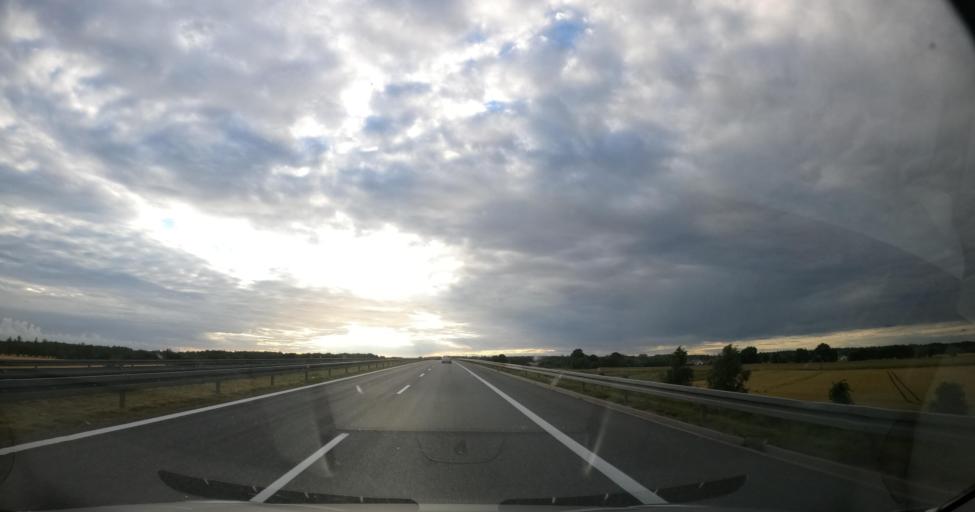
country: PL
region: Pomeranian Voivodeship
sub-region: Powiat slupski
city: Kobylnica
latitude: 54.4365
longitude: 16.9595
